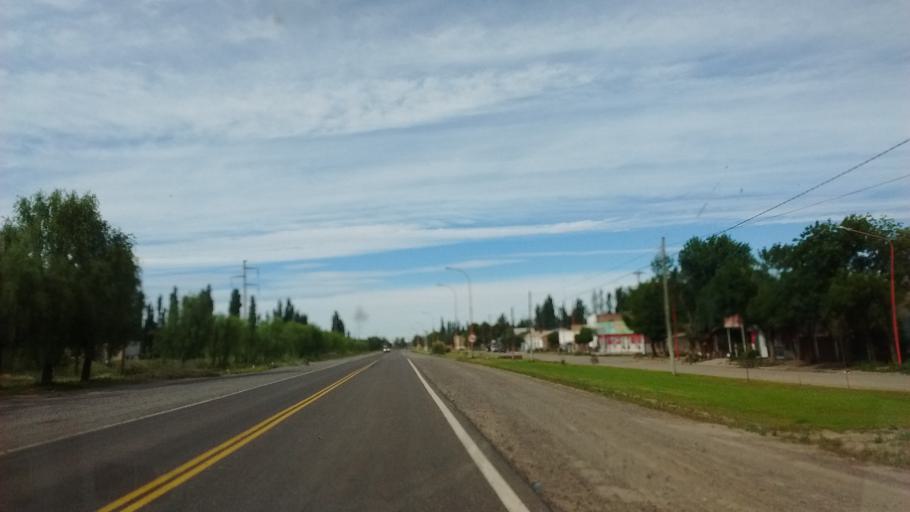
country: AR
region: Rio Negro
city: Contraalmirante Cordero
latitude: -38.6870
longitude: -68.1565
